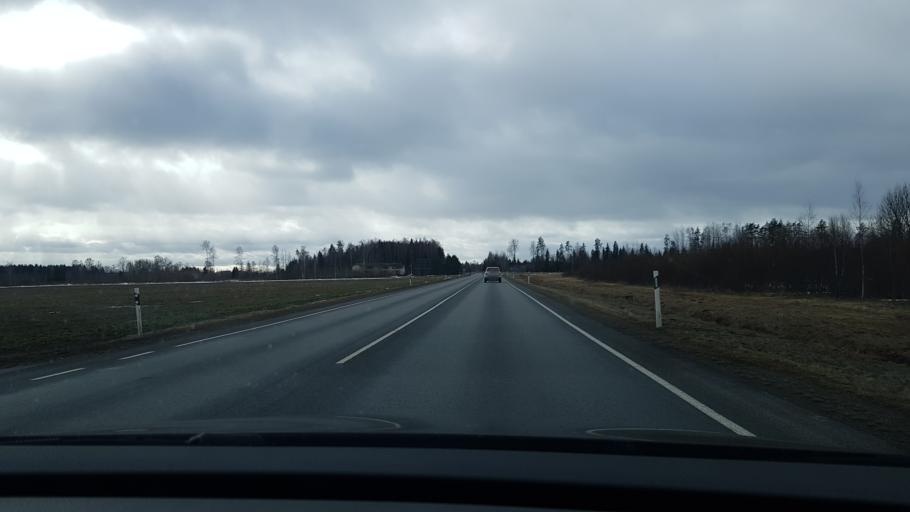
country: EE
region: Paernumaa
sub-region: Vaendra vald (alev)
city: Vandra
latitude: 58.6277
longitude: 24.9424
